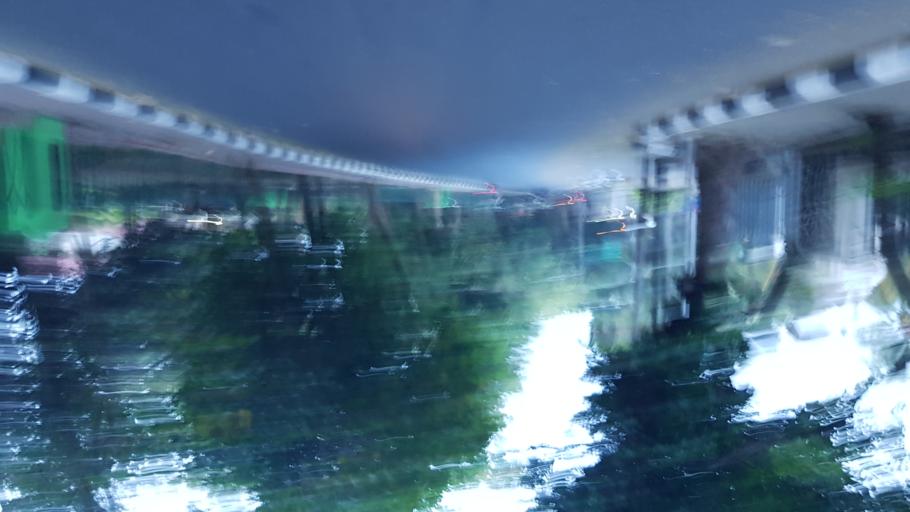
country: ID
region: West Java
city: Pamulang
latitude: -6.3151
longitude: 106.7917
